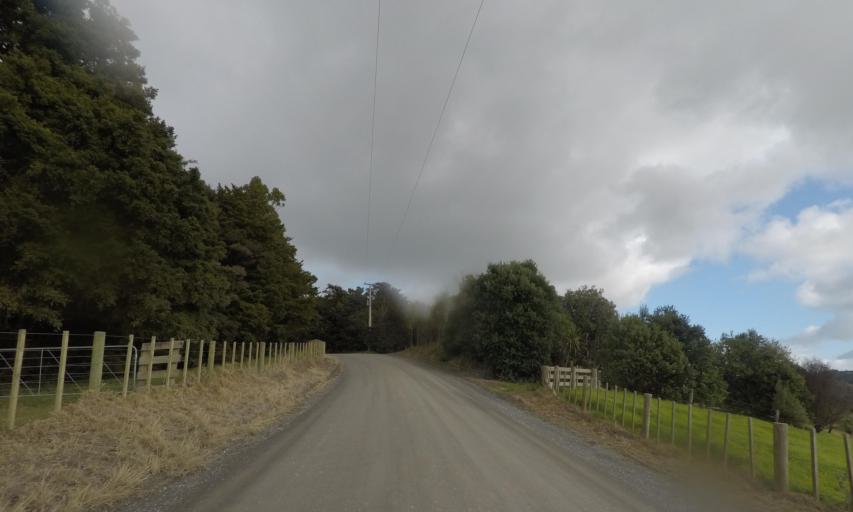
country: NZ
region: Auckland
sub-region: Auckland
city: Wellsford
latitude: -36.1689
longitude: 174.6021
